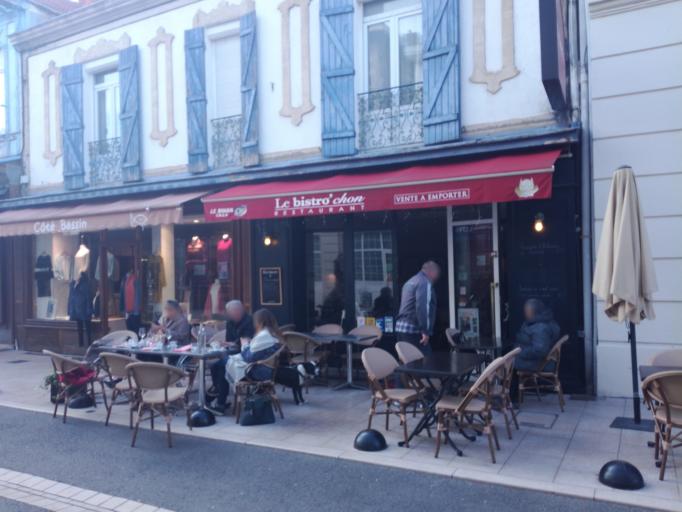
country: FR
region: Aquitaine
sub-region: Departement de la Gironde
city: Arcachon
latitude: 44.6607
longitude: -1.1727
